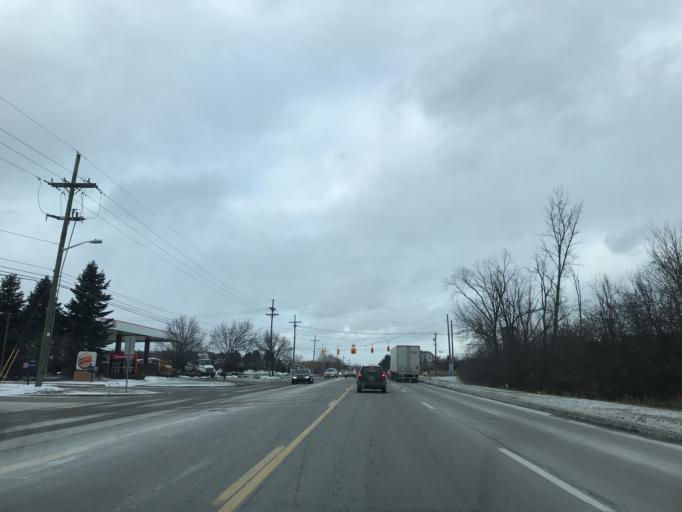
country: US
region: Michigan
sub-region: Wayne County
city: Plymouth
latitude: 42.3945
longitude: -83.4815
